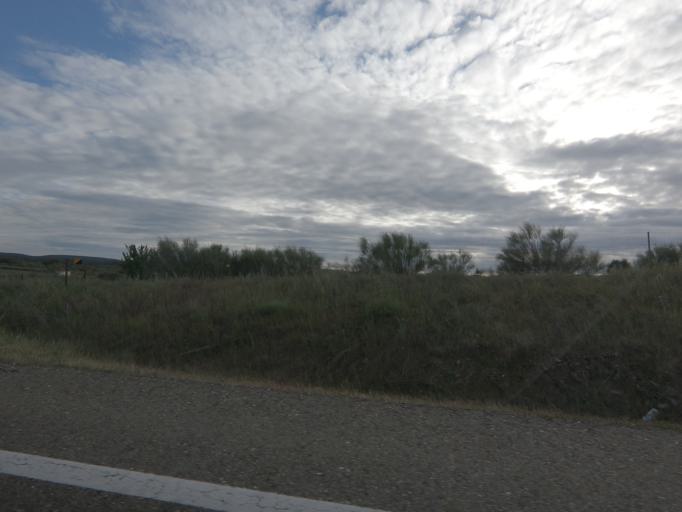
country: ES
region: Extremadura
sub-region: Provincia de Caceres
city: Torrejoncillo
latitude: 39.8888
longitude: -6.4797
